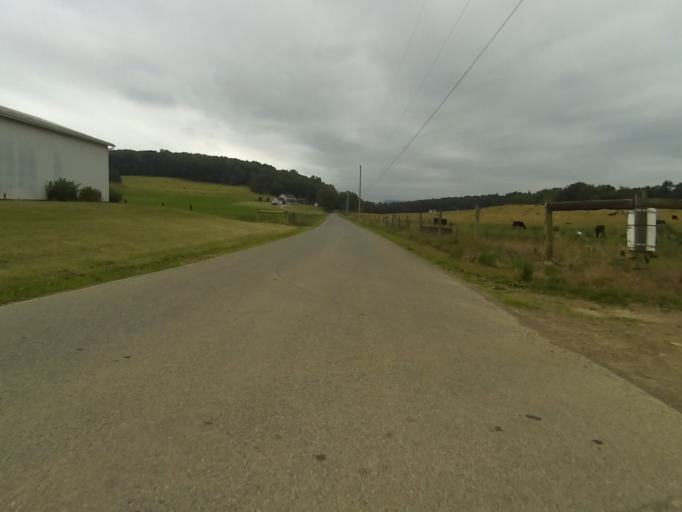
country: US
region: Pennsylvania
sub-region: Centre County
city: Stormstown
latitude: 40.6914
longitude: -78.0981
